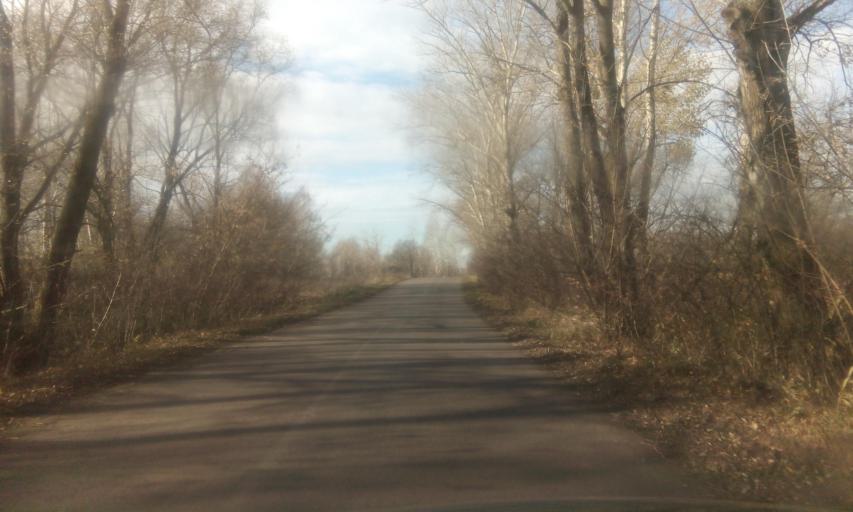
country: RU
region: Tula
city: Dubovka
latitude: 53.9573
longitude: 38.0580
